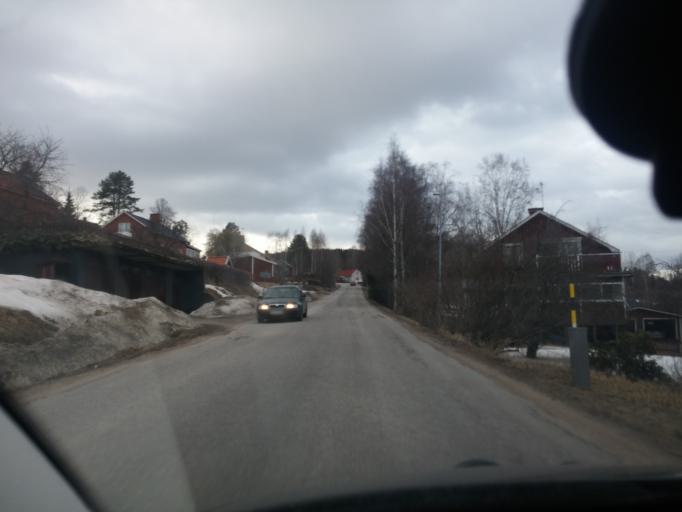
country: SE
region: Gaevleborg
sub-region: Ljusdals Kommun
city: Jaervsoe
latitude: 61.7225
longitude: 16.1669
